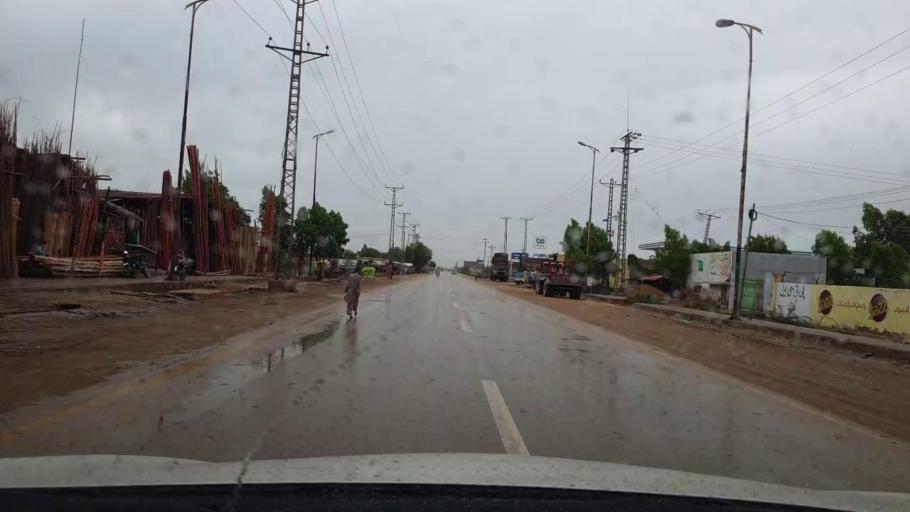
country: PK
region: Sindh
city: Kario
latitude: 24.6534
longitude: 68.5379
